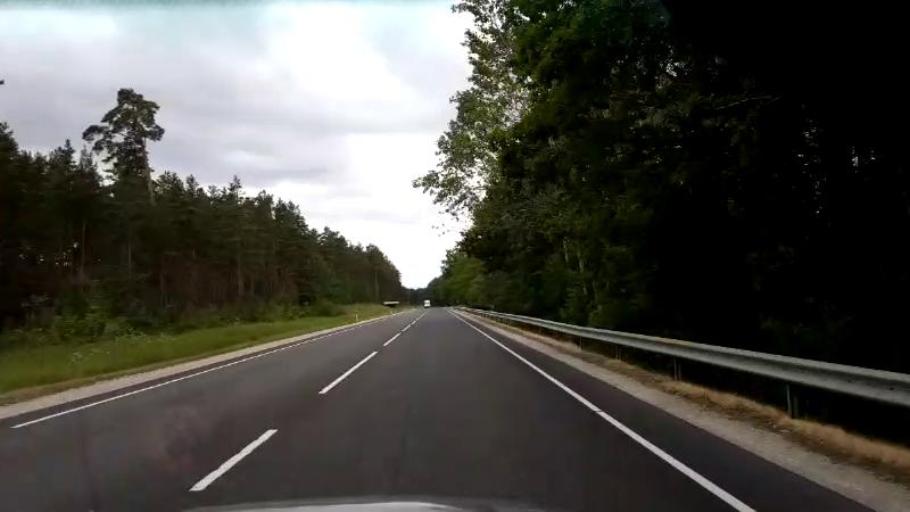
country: EE
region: Paernumaa
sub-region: Paernu linn
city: Parnu
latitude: 58.2671
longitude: 24.5522
